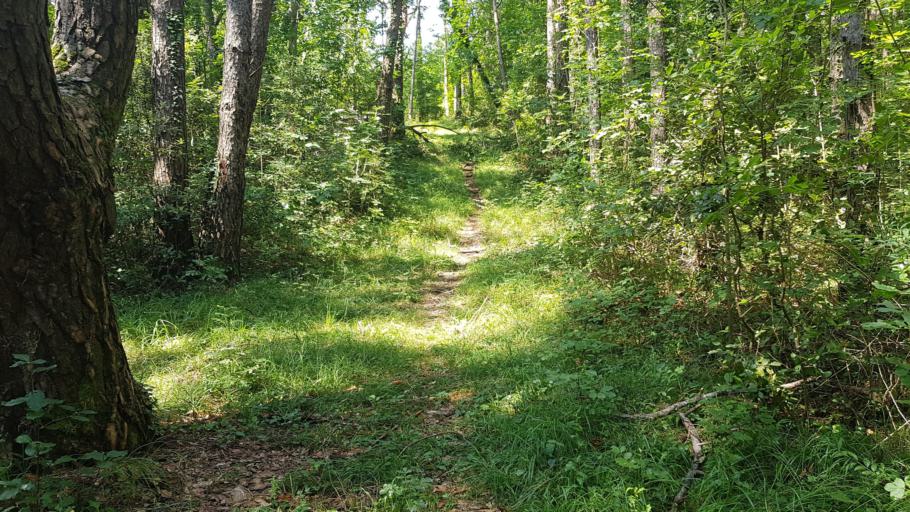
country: IT
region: Trentino-Alto Adige
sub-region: Provincia di Trento
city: Calavino
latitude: 46.0379
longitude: 10.9900
